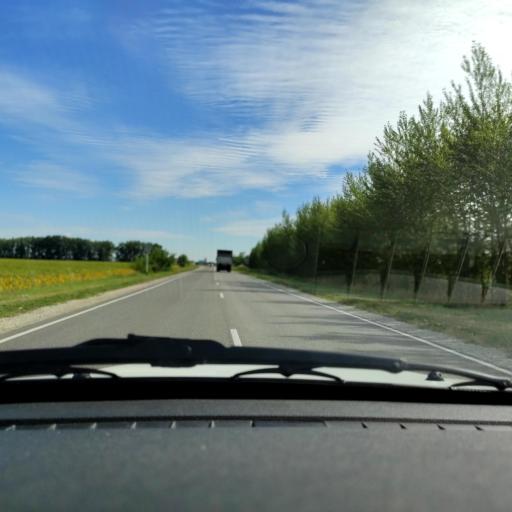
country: RU
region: Voronezj
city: Orlovo
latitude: 51.7321
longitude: 39.5599
